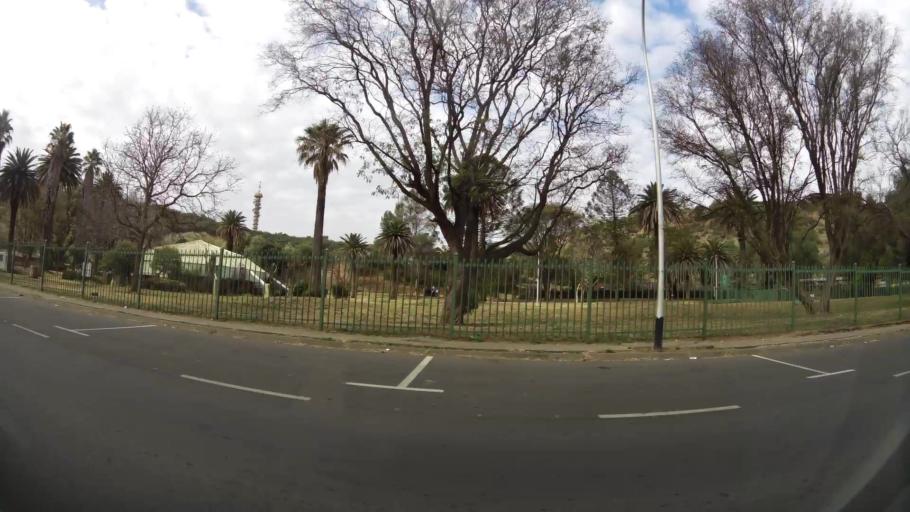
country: ZA
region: Orange Free State
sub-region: Mangaung Metropolitan Municipality
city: Bloemfontein
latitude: -29.1036
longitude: 26.2232
